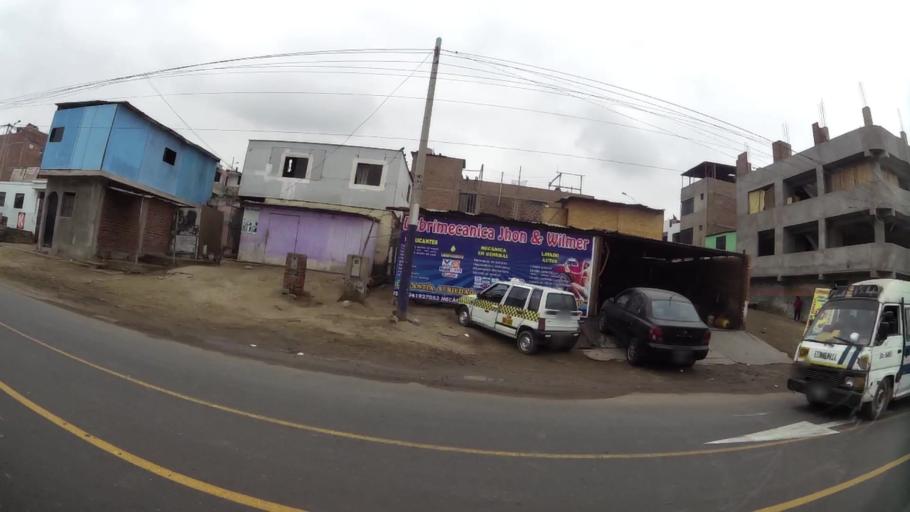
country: PE
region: Lima
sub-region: Lima
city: Surco
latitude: -12.1983
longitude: -76.9954
